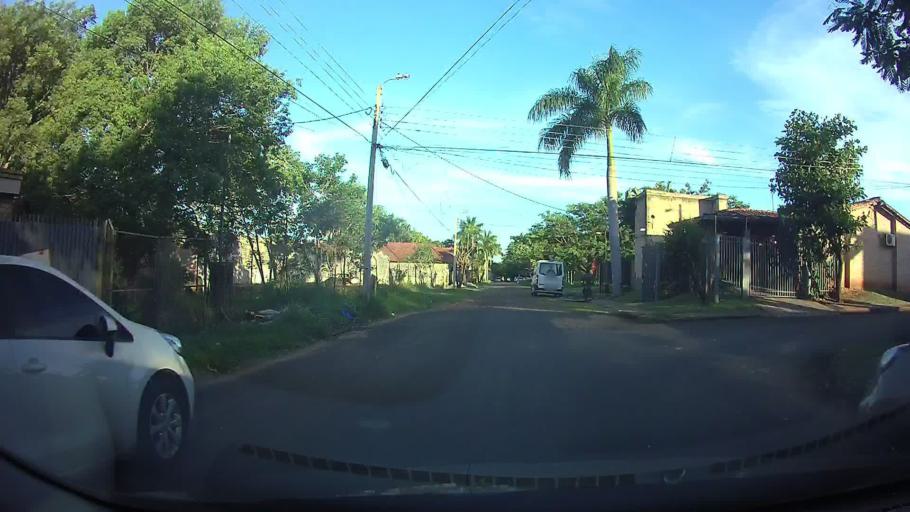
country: PY
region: Central
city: San Lorenzo
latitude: -25.2657
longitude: -57.5080
